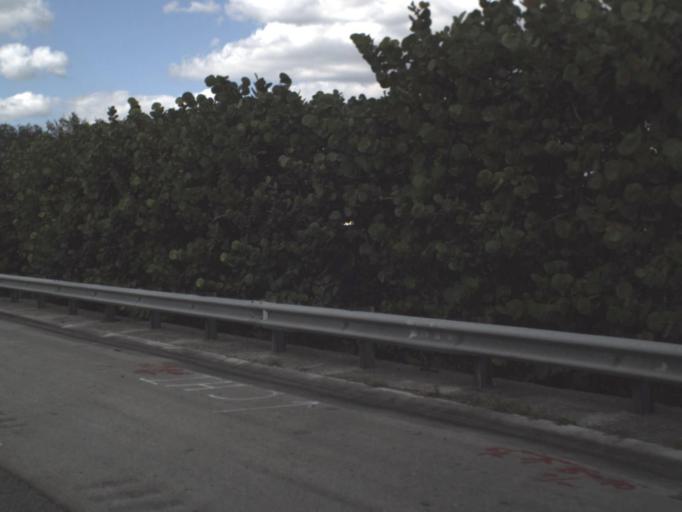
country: US
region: Florida
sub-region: Miami-Dade County
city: Scott Lake
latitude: 25.9442
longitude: -80.2247
